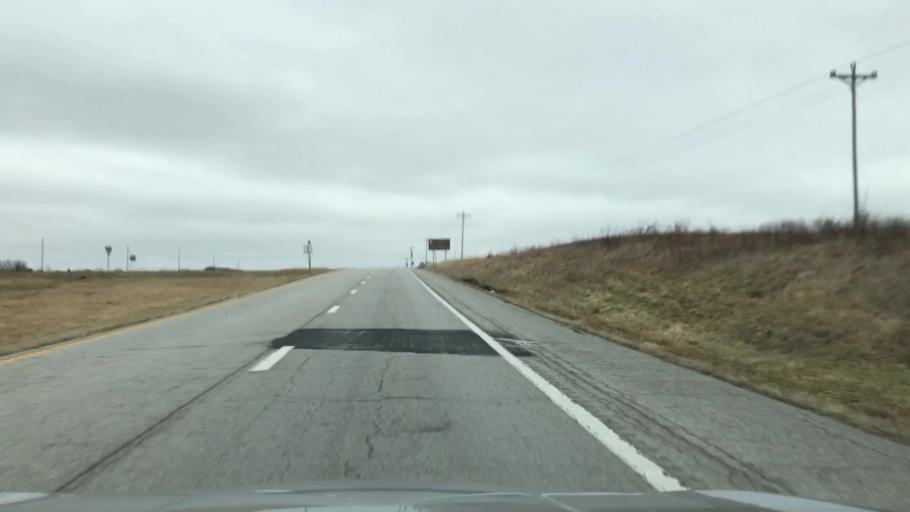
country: US
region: Missouri
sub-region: Linn County
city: Linneus
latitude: 39.7782
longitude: -93.1849
